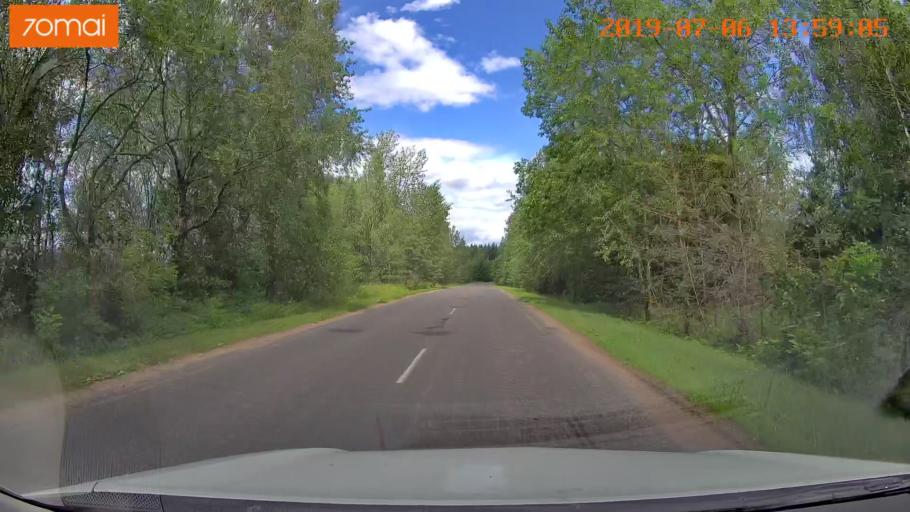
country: BY
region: Minsk
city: Ivyanyets
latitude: 53.7913
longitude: 26.8114
